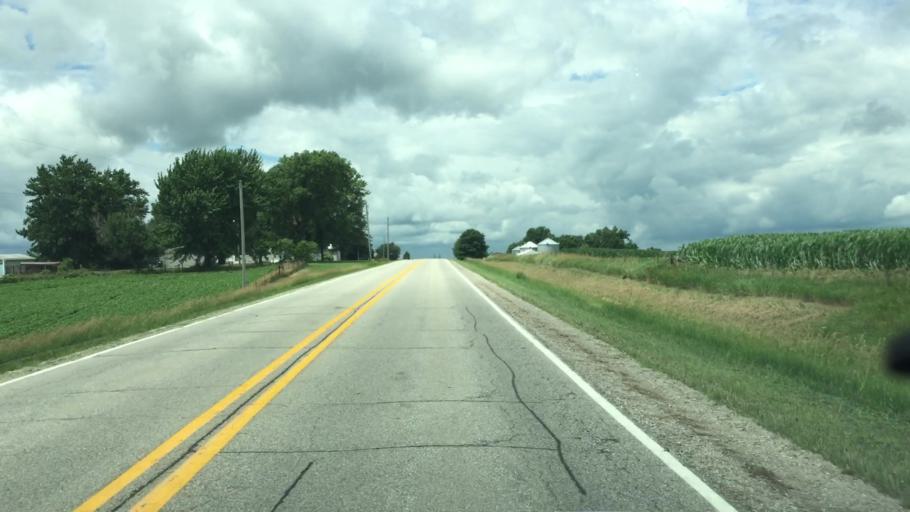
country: US
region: Iowa
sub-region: Jasper County
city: Monroe
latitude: 41.5736
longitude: -93.0845
